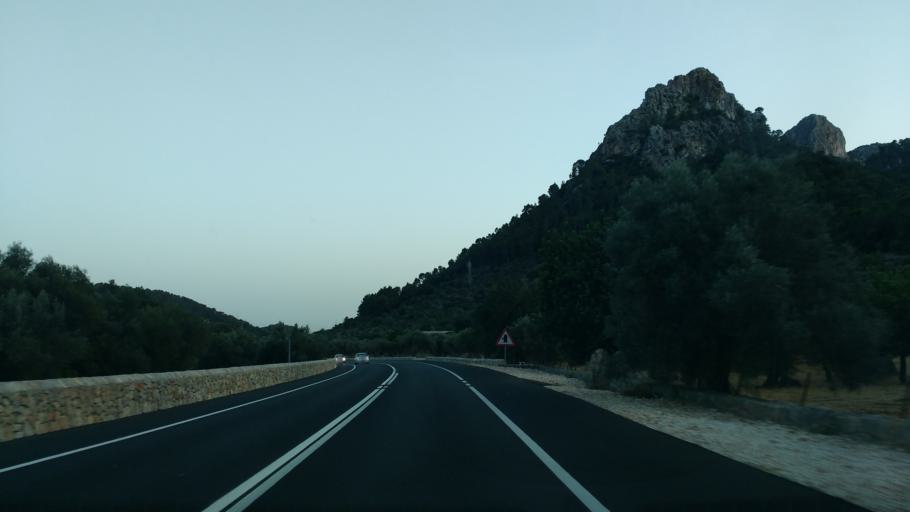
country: ES
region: Balearic Islands
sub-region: Illes Balears
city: Bunyola
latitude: 39.7094
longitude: 2.6890
